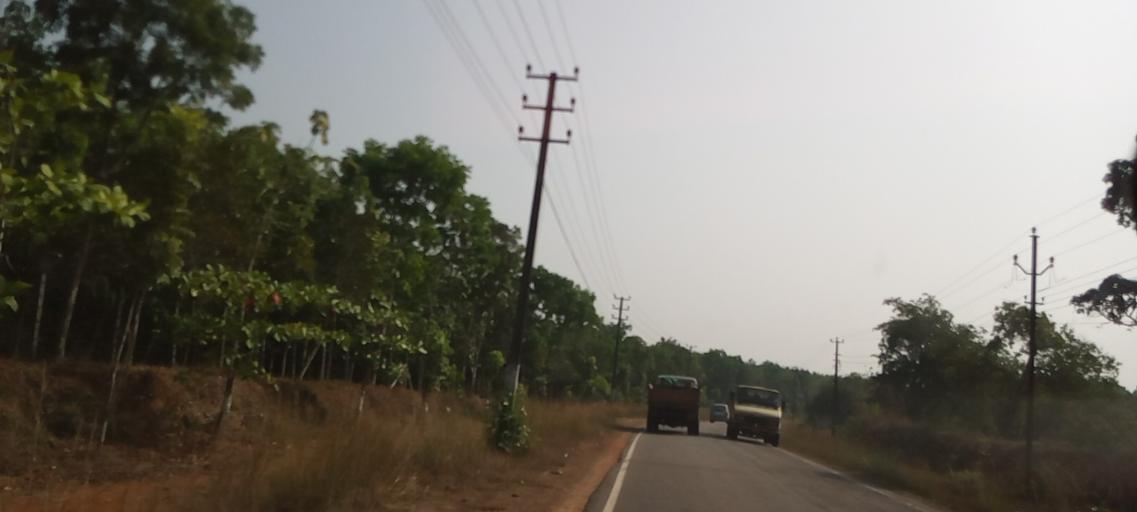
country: IN
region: Karnataka
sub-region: Udupi
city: Coondapoor
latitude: 13.5164
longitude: 74.7569
